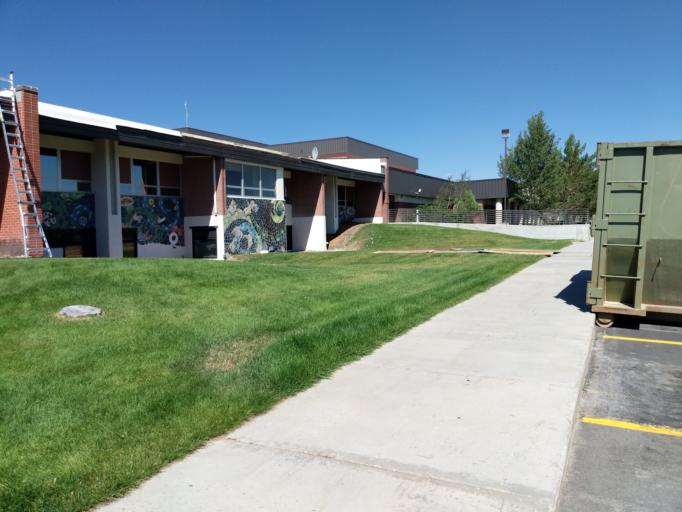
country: US
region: Wyoming
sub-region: Sublette County
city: Pinedale
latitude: 42.8703
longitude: -109.8598
